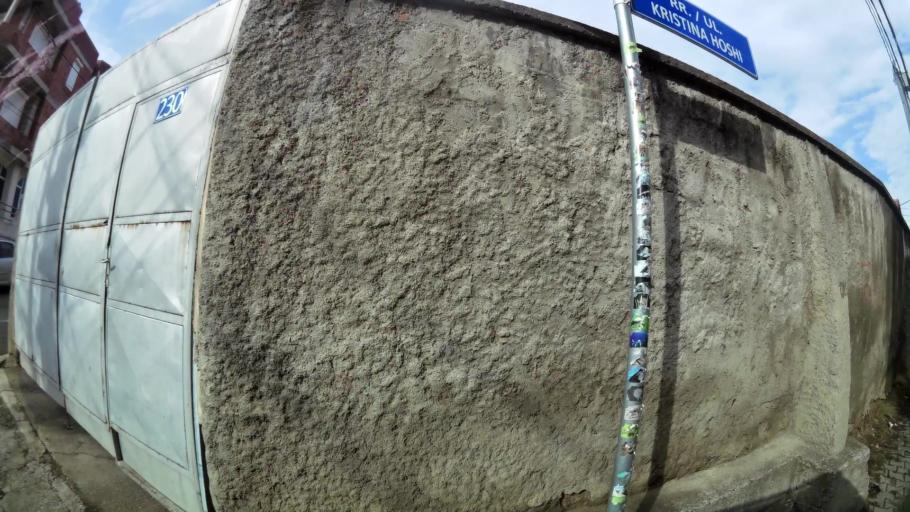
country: XK
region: Pristina
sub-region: Komuna e Prishtines
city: Pristina
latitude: 42.6755
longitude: 21.1576
